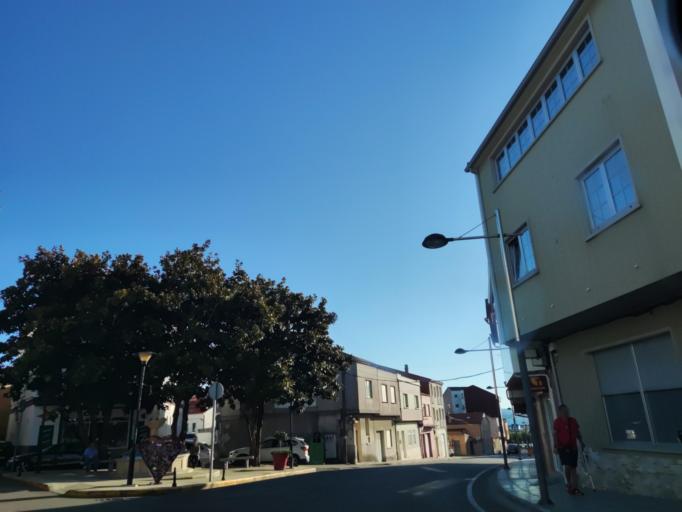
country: ES
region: Galicia
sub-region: Provincia da Coruna
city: Boiro
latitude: 42.6171
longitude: -8.8835
